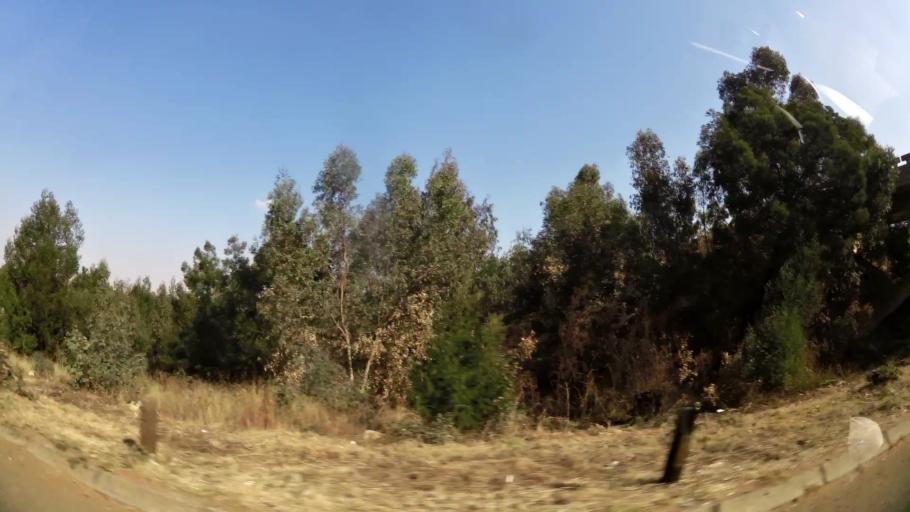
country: ZA
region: Gauteng
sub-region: West Rand District Municipality
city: Randfontein
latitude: -26.1811
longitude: 27.7210
